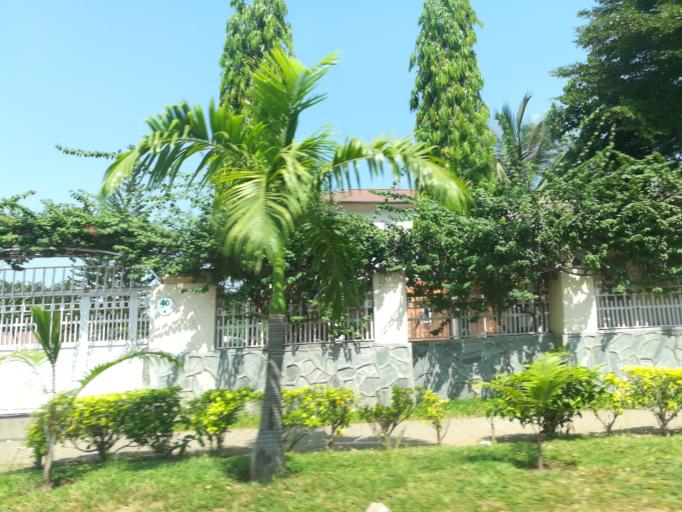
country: NG
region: Abuja Federal Capital Territory
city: Abuja
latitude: 9.0757
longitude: 7.4282
